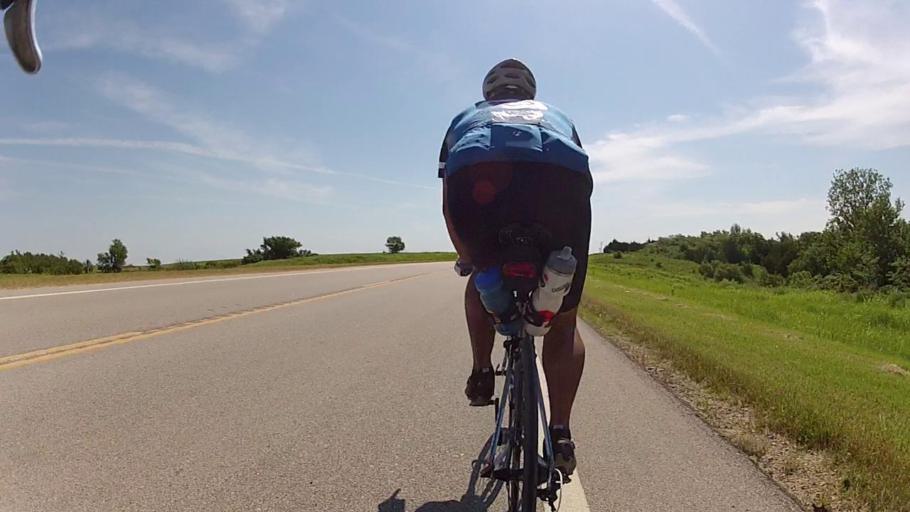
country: US
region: Kansas
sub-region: Chautauqua County
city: Sedan
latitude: 37.1099
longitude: -96.5298
